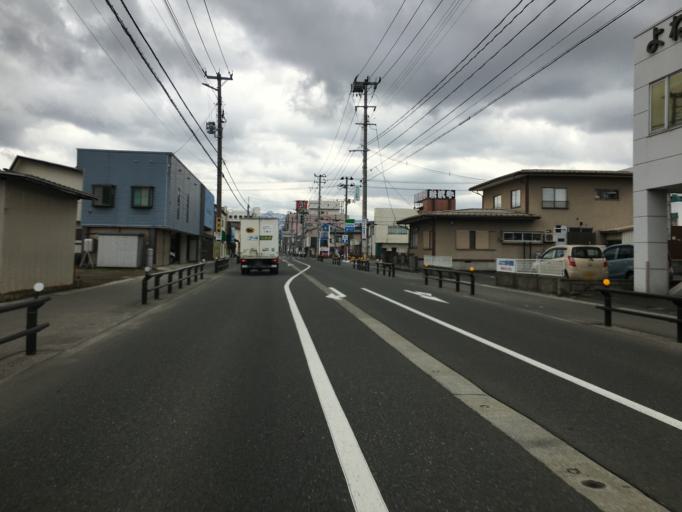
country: JP
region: Yamagata
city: Yonezawa
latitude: 37.9154
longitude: 140.1137
